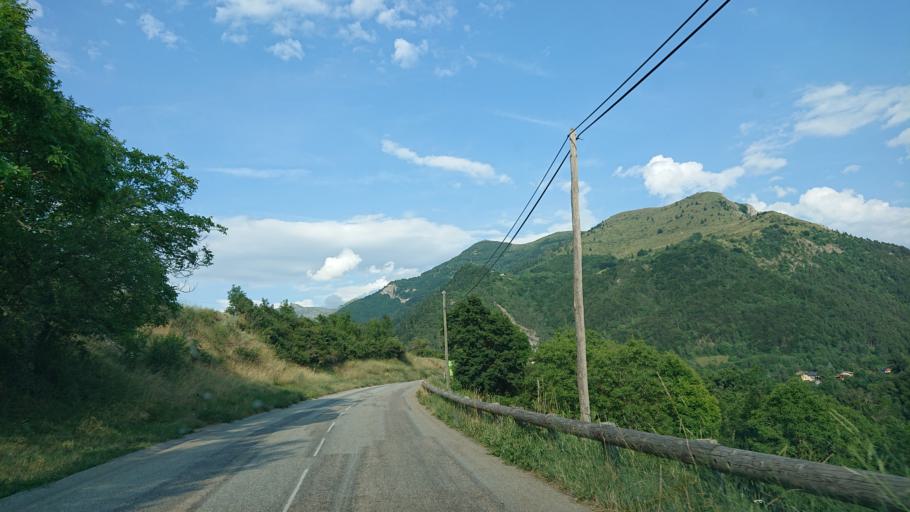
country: FR
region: Rhone-Alpes
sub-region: Departement de l'Isere
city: La Mure
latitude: 44.8189
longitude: 5.9376
